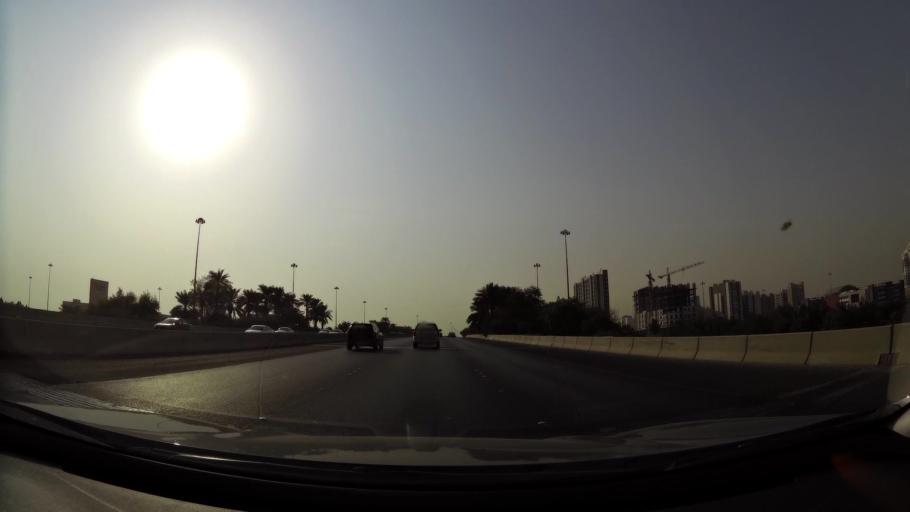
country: KW
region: Muhafazat Hawalli
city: Salwa
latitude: 29.2705
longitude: 48.0841
